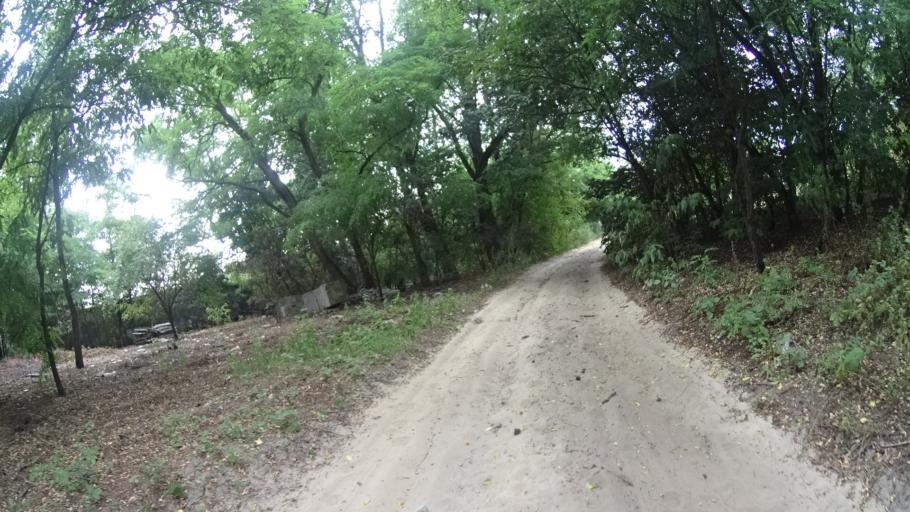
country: PL
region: Masovian Voivodeship
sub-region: Powiat bialobrzeski
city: Wysmierzyce
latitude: 51.6526
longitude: 20.7872
